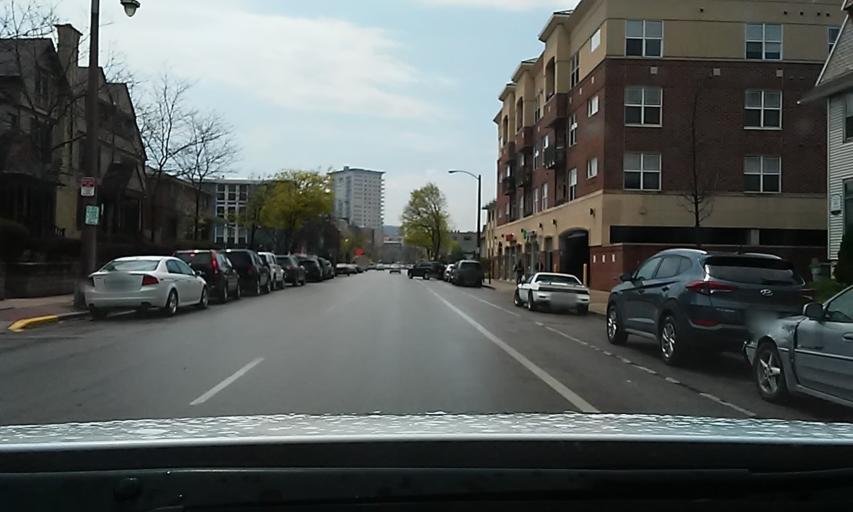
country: US
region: Wisconsin
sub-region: Milwaukee County
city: Milwaukee
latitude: 43.0521
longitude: -87.8931
